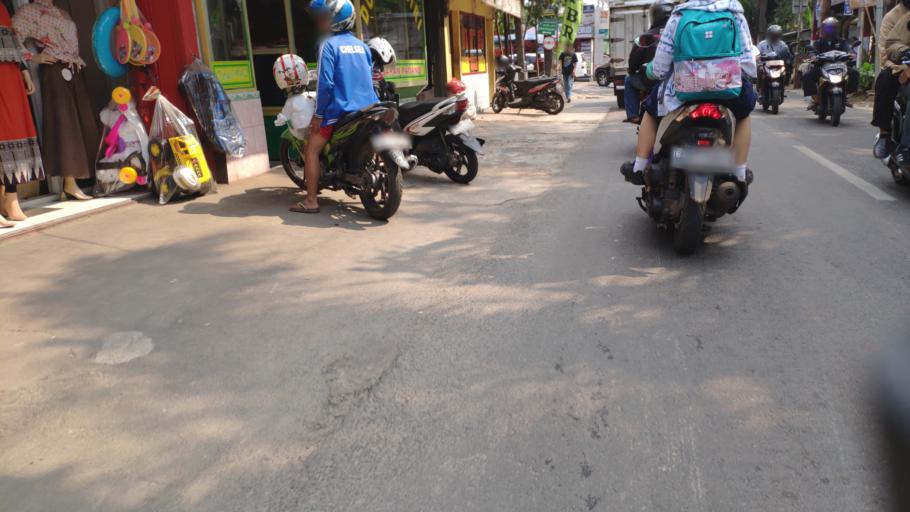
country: ID
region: West Java
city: Depok
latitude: -6.3089
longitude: 106.8271
